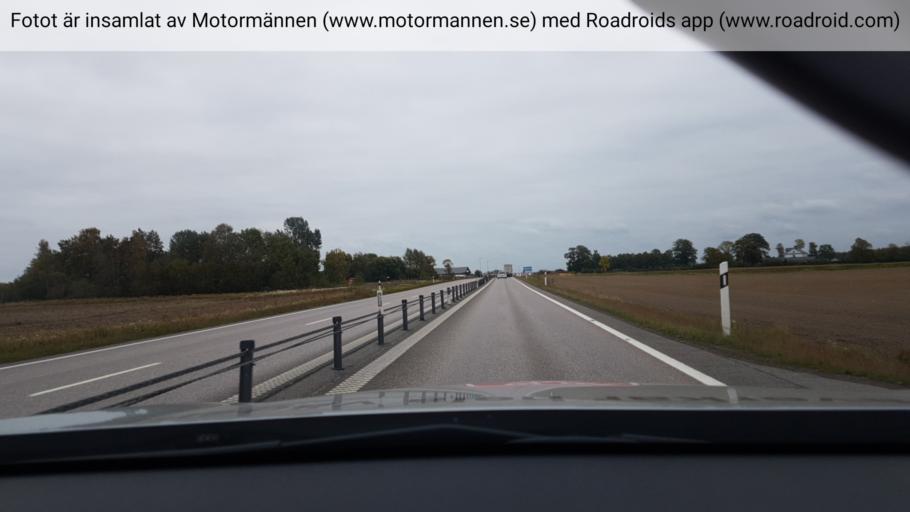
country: SE
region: Vaestra Goetaland
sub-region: Skara Kommun
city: Skara
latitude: 58.3713
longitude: 13.3707
